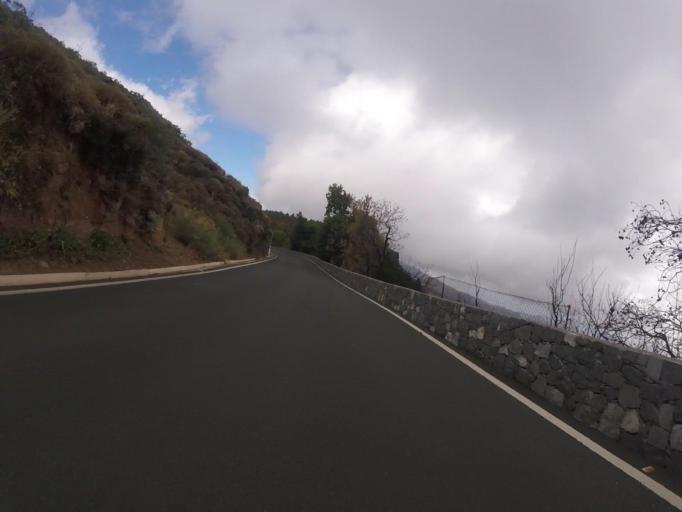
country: ES
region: Canary Islands
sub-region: Provincia de Las Palmas
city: San Bartolome
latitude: 27.9708
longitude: -15.5722
